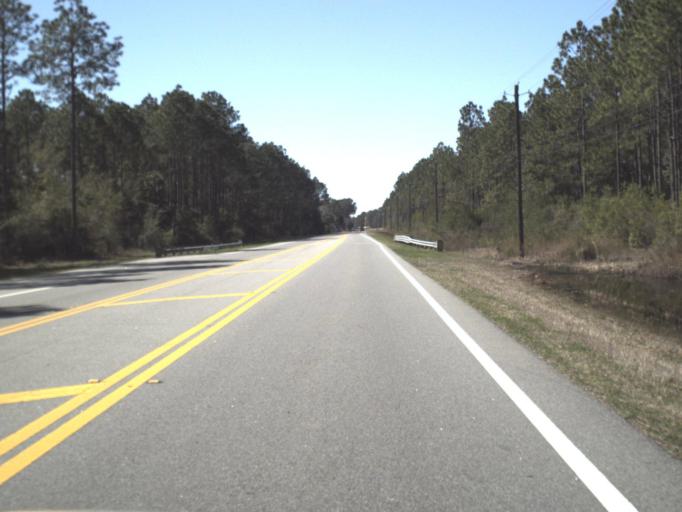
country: US
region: Florida
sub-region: Bay County
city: Laguna Beach
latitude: 30.2987
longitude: -85.8426
